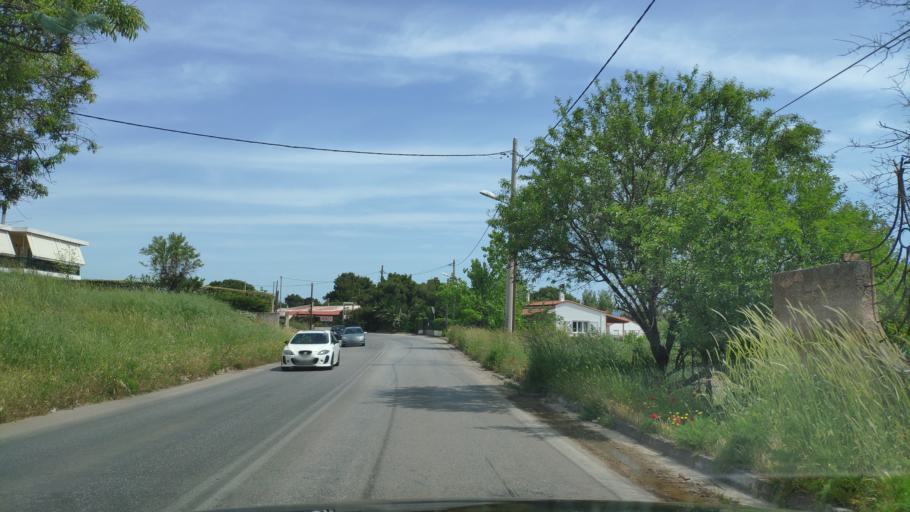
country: GR
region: Attica
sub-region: Nomarchia Anatolikis Attikis
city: Agios Stefanos
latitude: 38.1534
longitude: 23.8577
